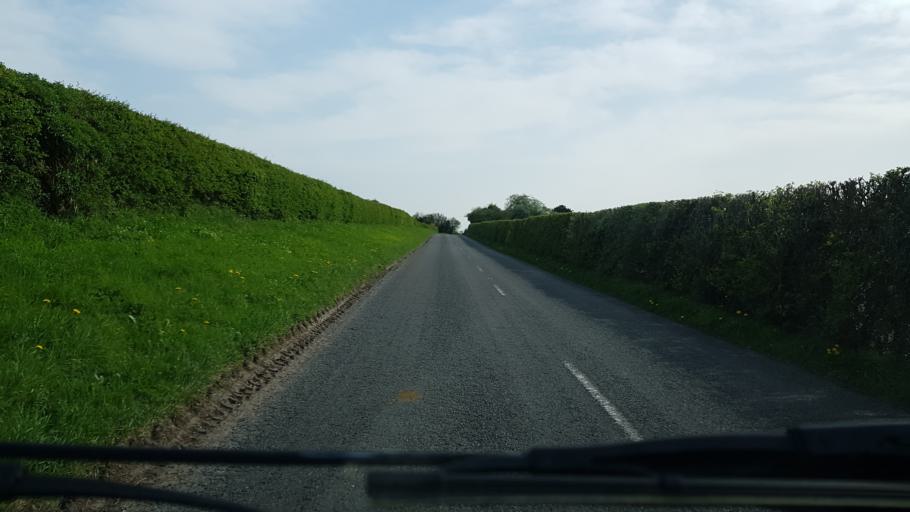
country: GB
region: England
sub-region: Hampshire
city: Overton
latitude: 51.2642
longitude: -1.2645
